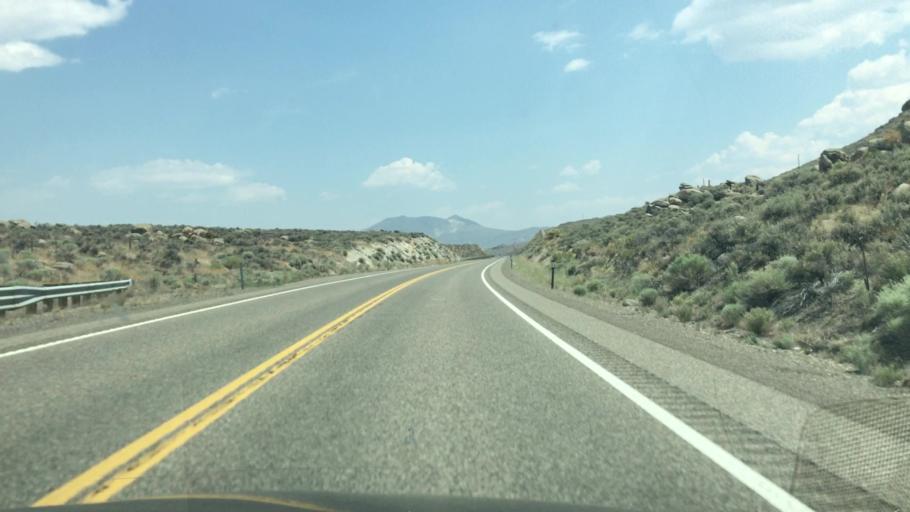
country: US
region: Nevada
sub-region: Elko County
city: Jackpot
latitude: 41.7374
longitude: -114.7861
